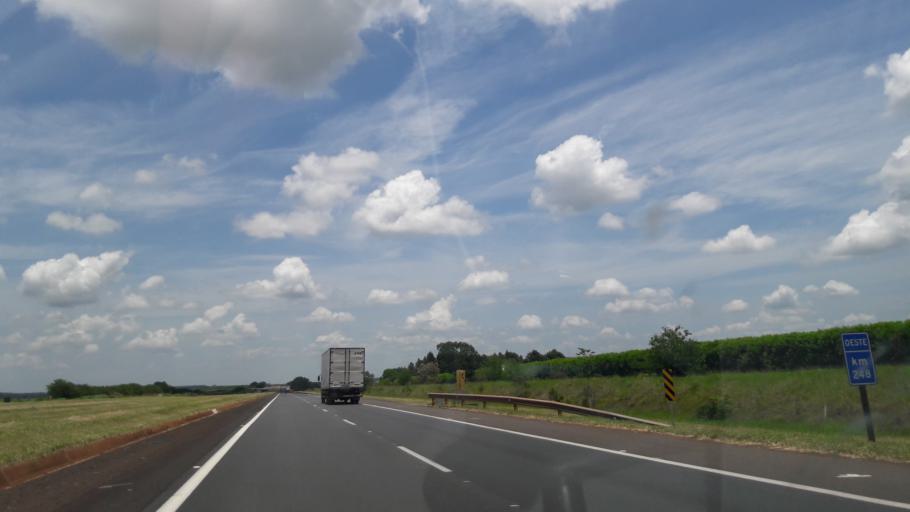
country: BR
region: Sao Paulo
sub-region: Avare
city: Avare
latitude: -22.9538
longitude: -48.8699
